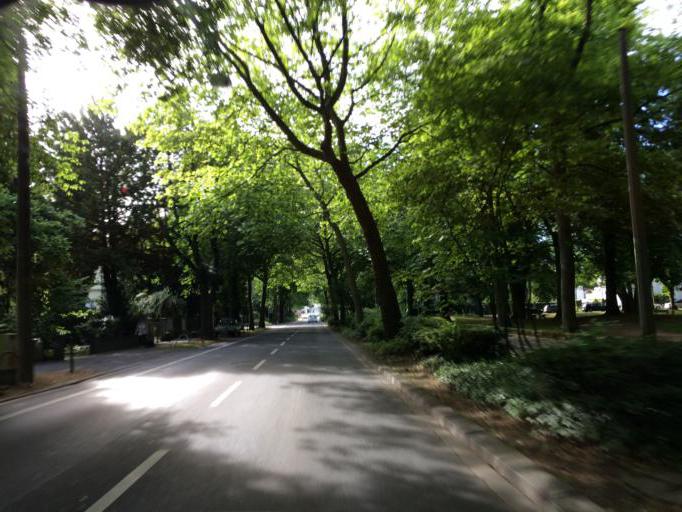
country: DE
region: North Rhine-Westphalia
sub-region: Regierungsbezirk Koln
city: Konigswinter
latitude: 50.6823
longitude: 7.1585
